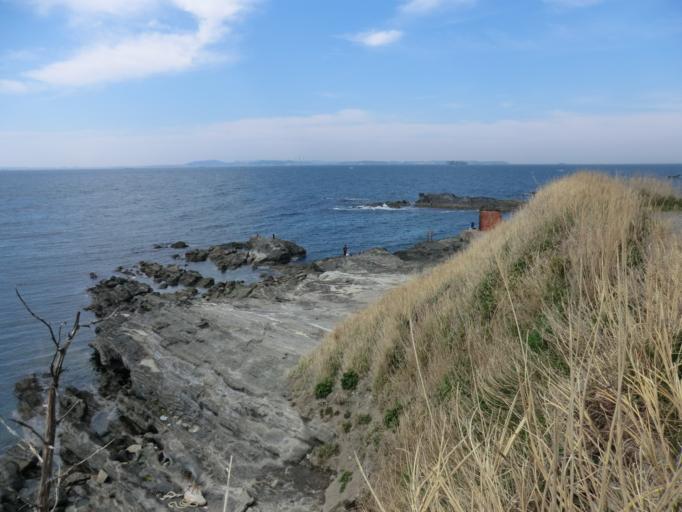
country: JP
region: Chiba
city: Futtsu
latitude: 35.1550
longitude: 139.8188
